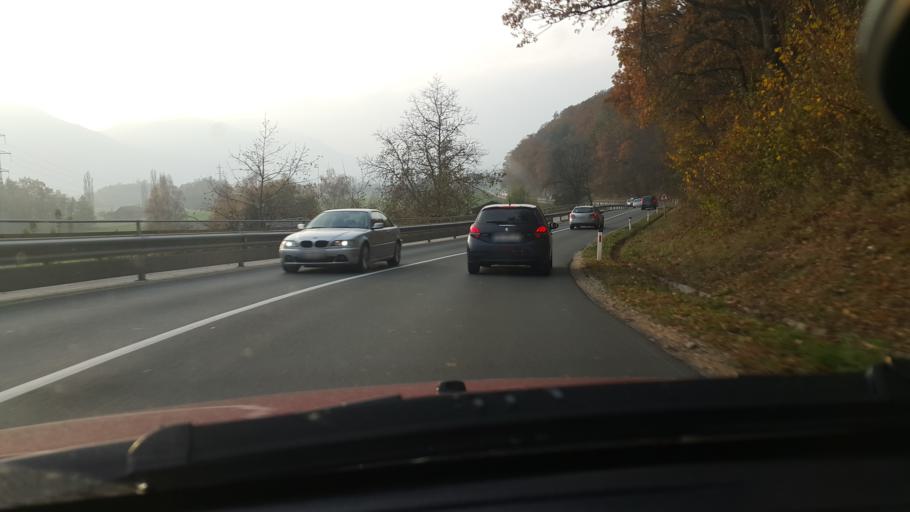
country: SI
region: Slovenska Konjice
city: Slovenske Konjice
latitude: 46.3398
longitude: 15.4661
